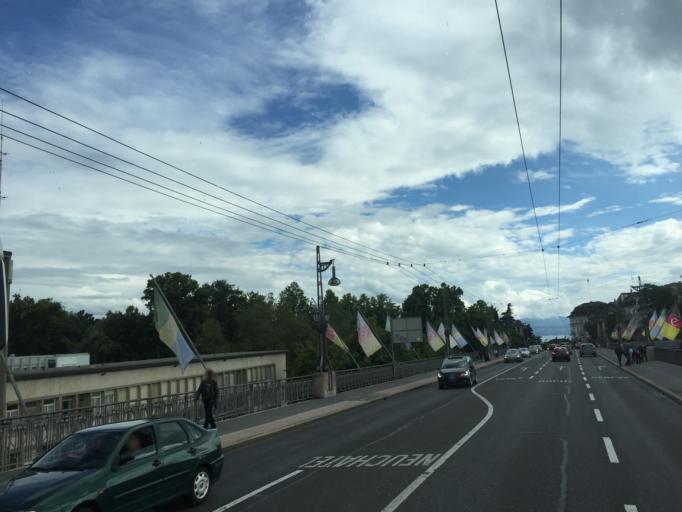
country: CH
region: Vaud
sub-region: Lausanne District
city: Lausanne
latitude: 46.5227
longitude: 6.6242
